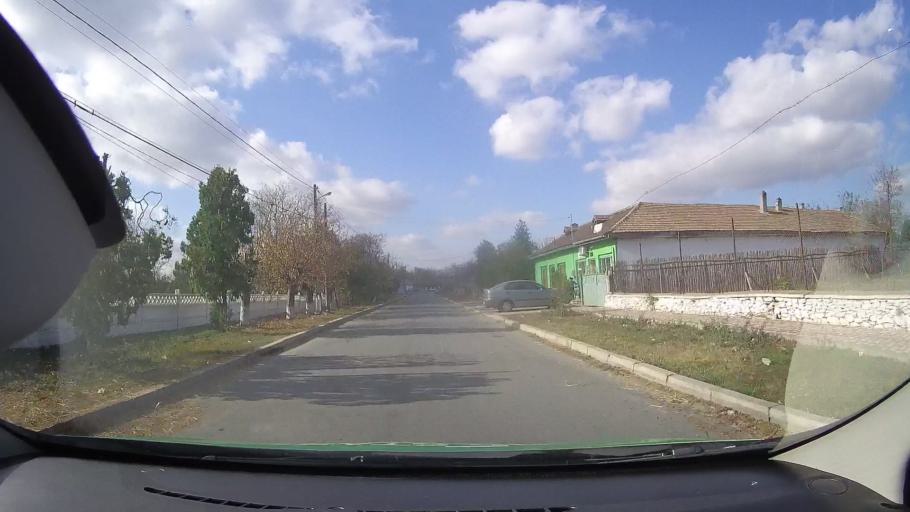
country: RO
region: Constanta
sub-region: Comuna Istria
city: Istria
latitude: 44.5725
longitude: 28.7101
